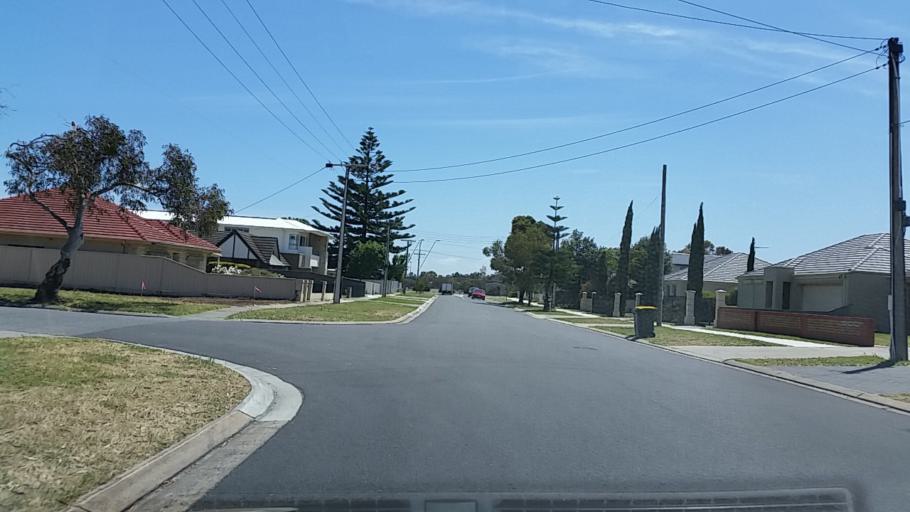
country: AU
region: South Australia
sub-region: Charles Sturt
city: Grange
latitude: -34.8987
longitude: 138.4922
